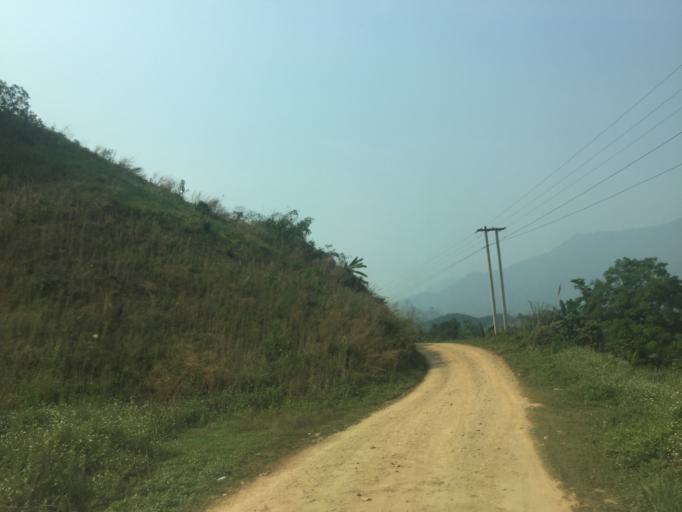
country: TH
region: Phayao
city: Phu Sang
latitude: 19.6483
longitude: 100.5259
